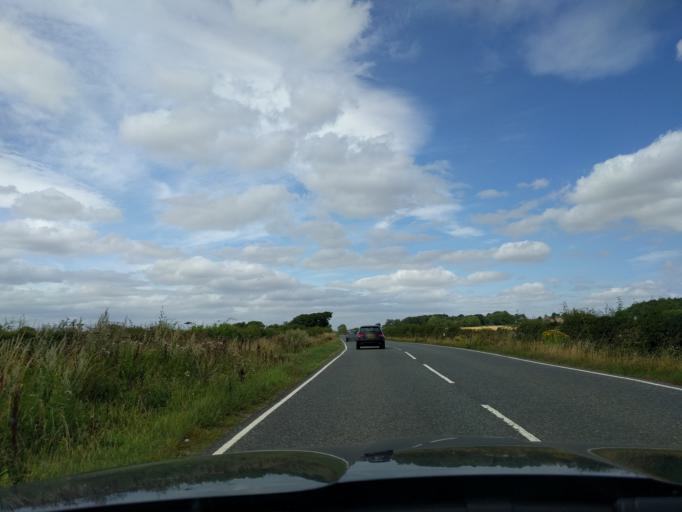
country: GB
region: England
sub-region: Northumberland
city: Bedlington
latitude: 55.1225
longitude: -1.6303
